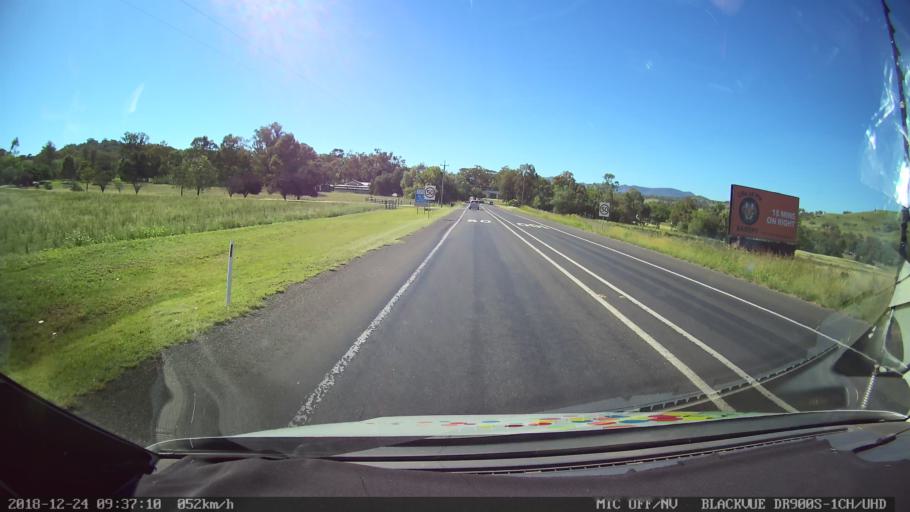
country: AU
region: New South Wales
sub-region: Liverpool Plains
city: Quirindi
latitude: -31.6431
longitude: 150.7247
